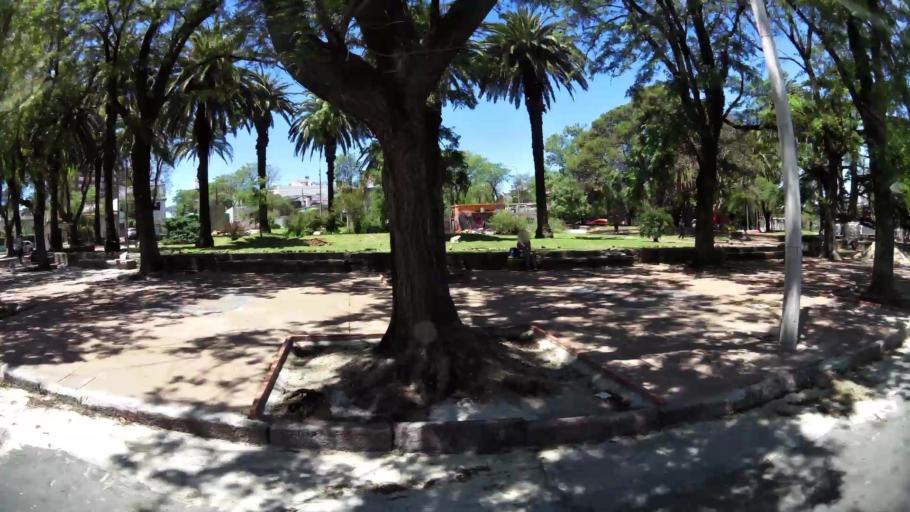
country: UY
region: Canelones
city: Paso de Carrasco
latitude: -34.8937
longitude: -56.1154
